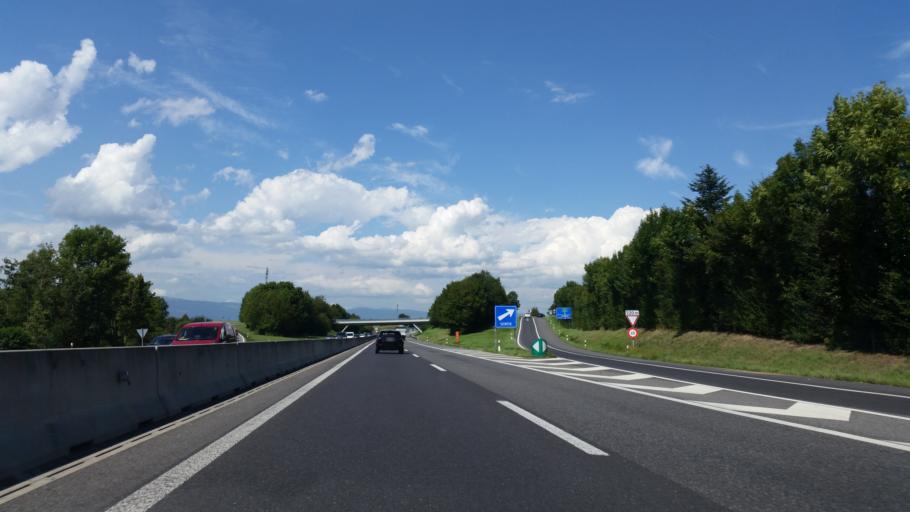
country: CH
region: Vaud
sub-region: Gros-de-Vaud District
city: Penthalaz
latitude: 46.5949
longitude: 6.5538
